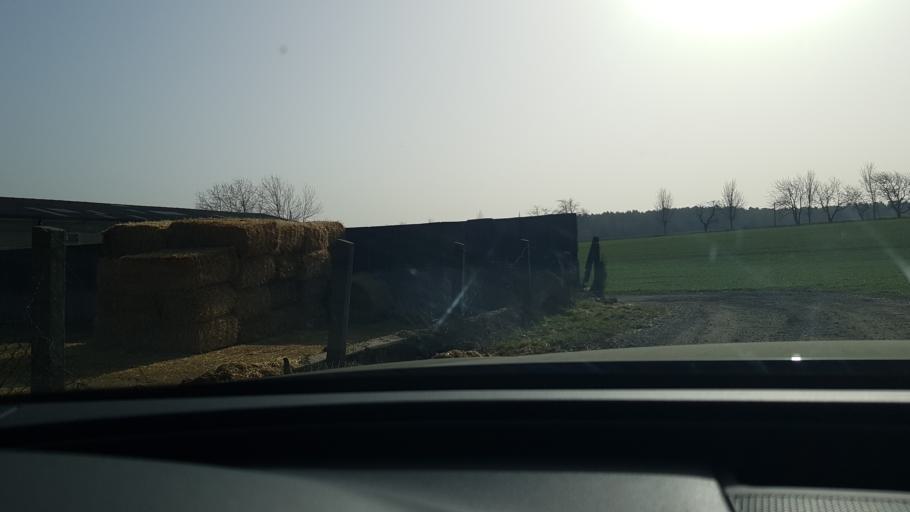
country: DE
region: Brandenburg
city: Schenkendobern
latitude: 51.9574
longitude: 14.6277
